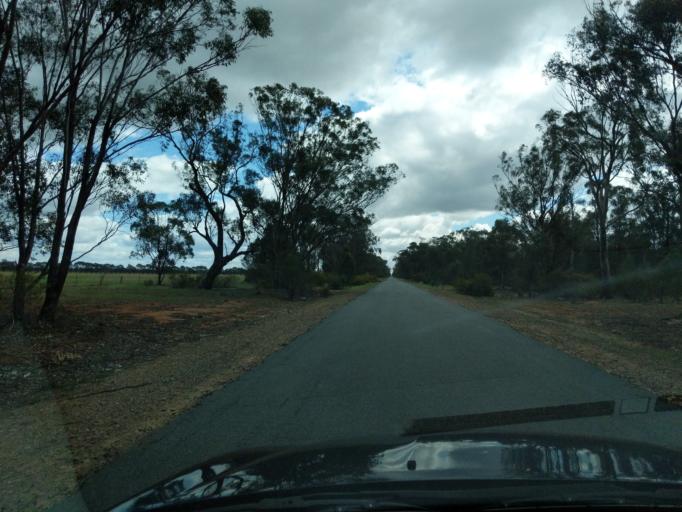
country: AU
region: New South Wales
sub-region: Coolamon
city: Coolamon
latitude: -34.9371
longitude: 146.9687
